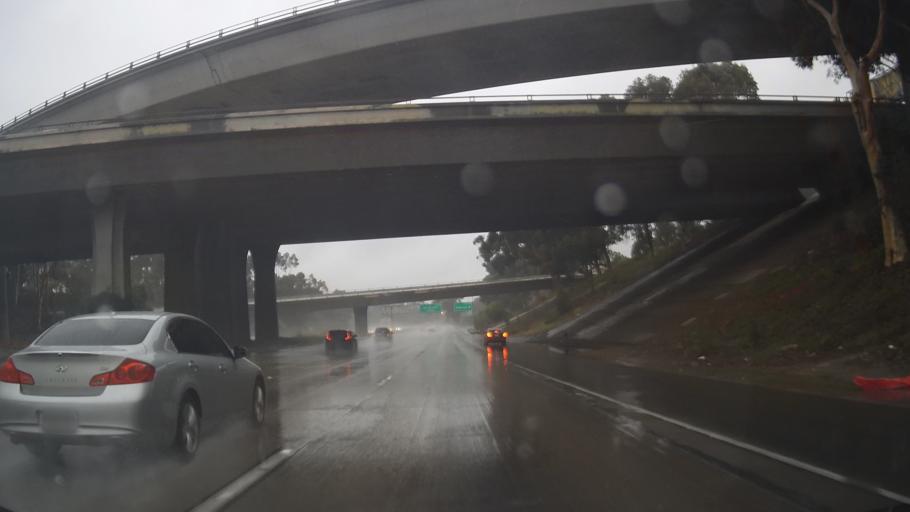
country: US
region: California
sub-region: San Diego County
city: National City
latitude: 32.7186
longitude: -117.1027
